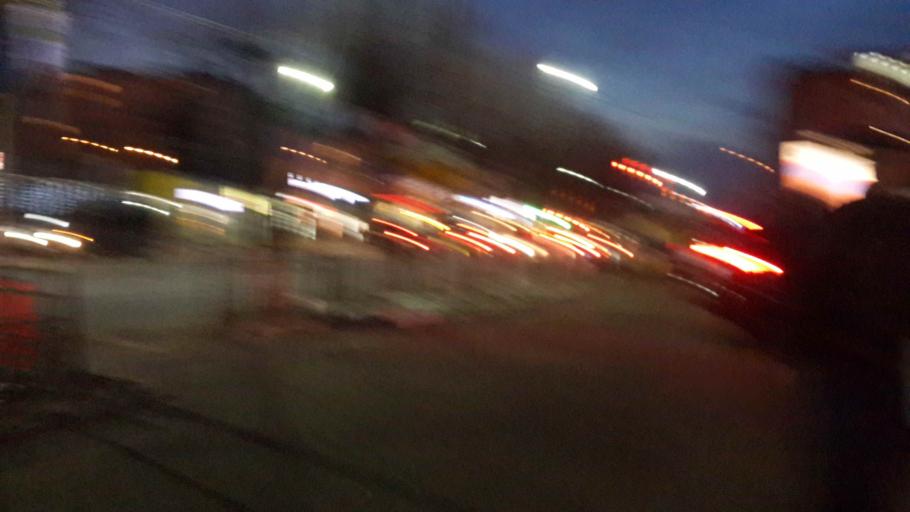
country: RU
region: Tula
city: Tula
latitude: 54.1971
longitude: 37.6030
